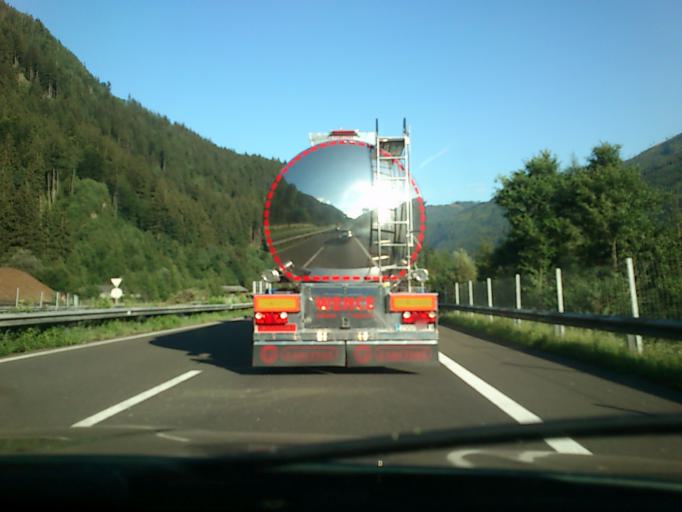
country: AT
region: Styria
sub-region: Politischer Bezirk Leoben
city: Wald am Schoberpass
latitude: 47.4350
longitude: 14.7006
